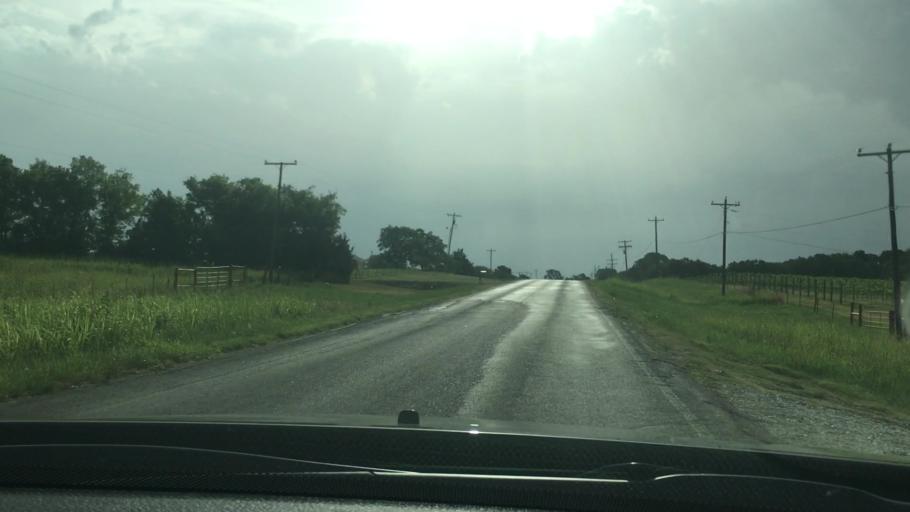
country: US
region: Oklahoma
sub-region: Pontotoc County
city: Byng
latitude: 34.8648
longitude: -96.6079
